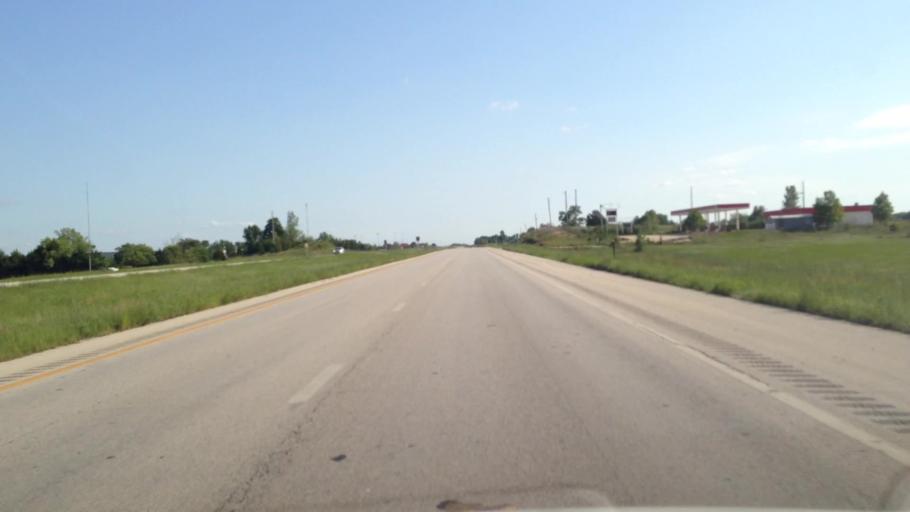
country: US
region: Kansas
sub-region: Bourbon County
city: Fort Scott
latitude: 37.7995
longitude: -94.7052
